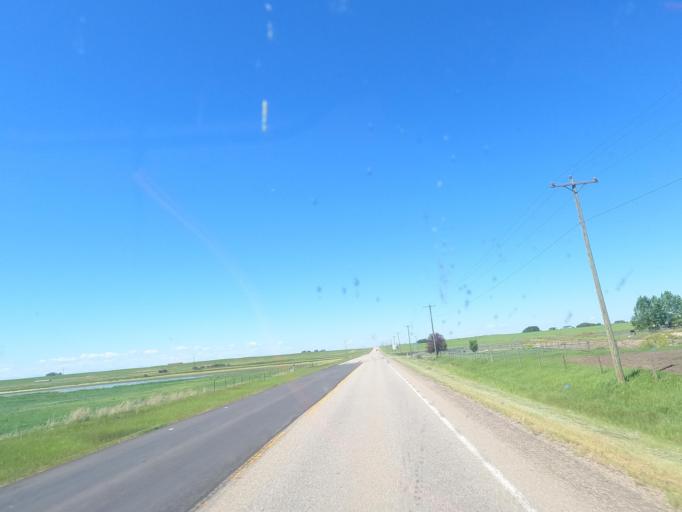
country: CA
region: Alberta
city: Chestermere
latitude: 51.1544
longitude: -113.8846
